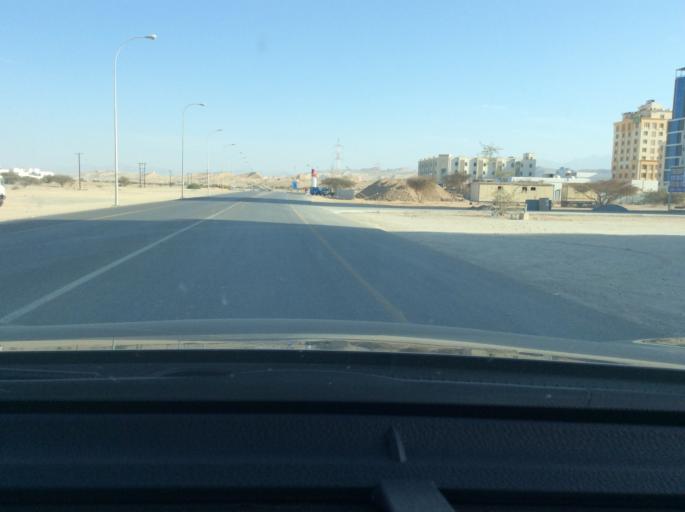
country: OM
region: Muhafazat Masqat
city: As Sib al Jadidah
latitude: 23.5765
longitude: 58.1817
